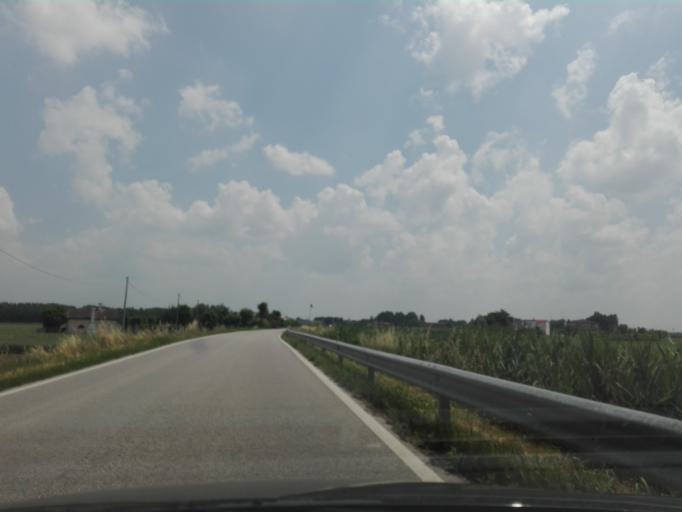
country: IT
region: Veneto
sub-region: Provincia di Rovigo
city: Adria
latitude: 45.0572
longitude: 12.0192
